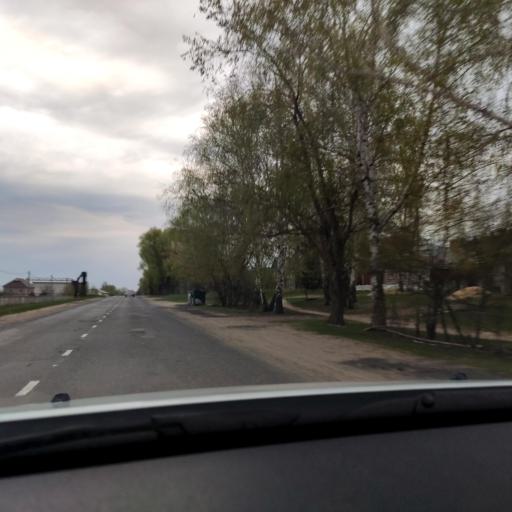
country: RU
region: Lipetsk
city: Zadonsk
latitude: 52.4065
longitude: 38.9216
